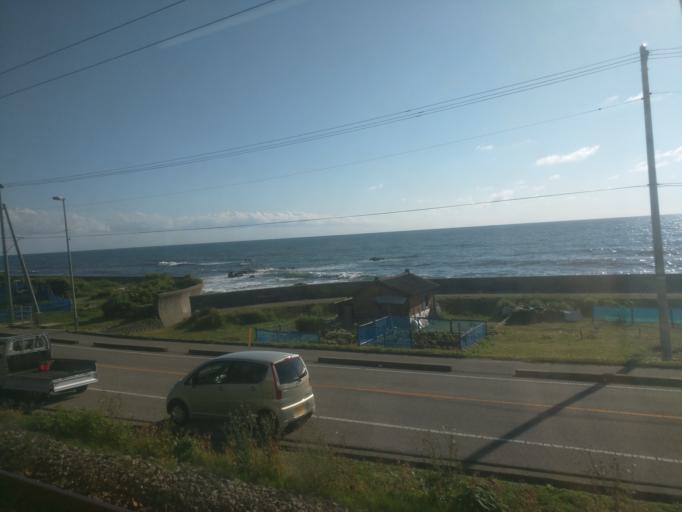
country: JP
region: Niigata
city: Murakami
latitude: 38.3367
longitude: 139.4531
